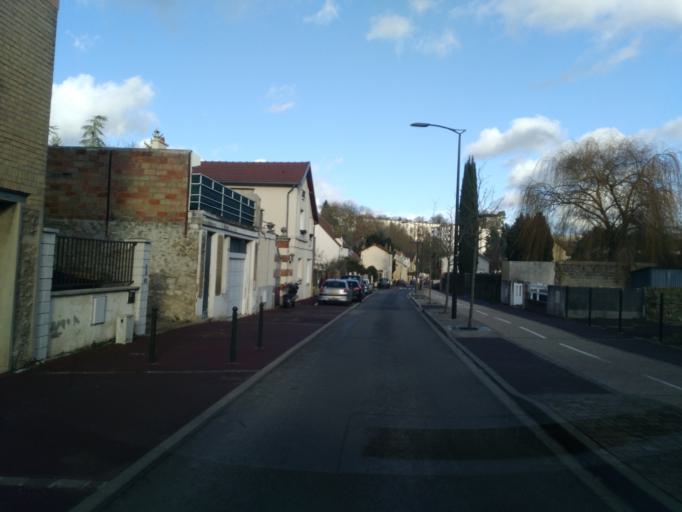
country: FR
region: Ile-de-France
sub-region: Departement des Yvelines
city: Fourqueux
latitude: 48.8966
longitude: 2.0675
